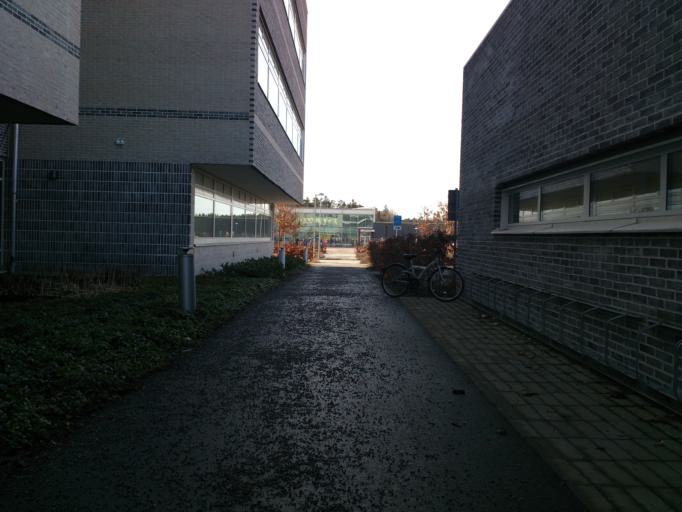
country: SE
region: Uppsala
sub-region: Uppsala Kommun
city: Saevja
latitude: 59.8167
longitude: 17.6597
